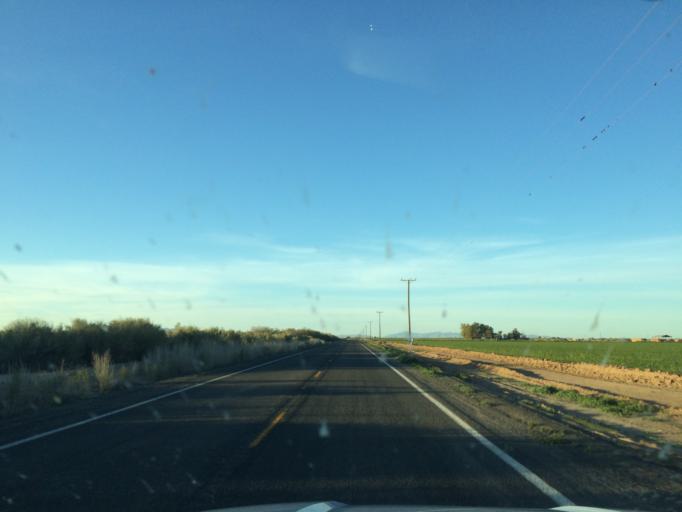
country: US
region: California
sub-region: Riverside County
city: Mesa Verde
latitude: 33.3673
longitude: -114.7219
